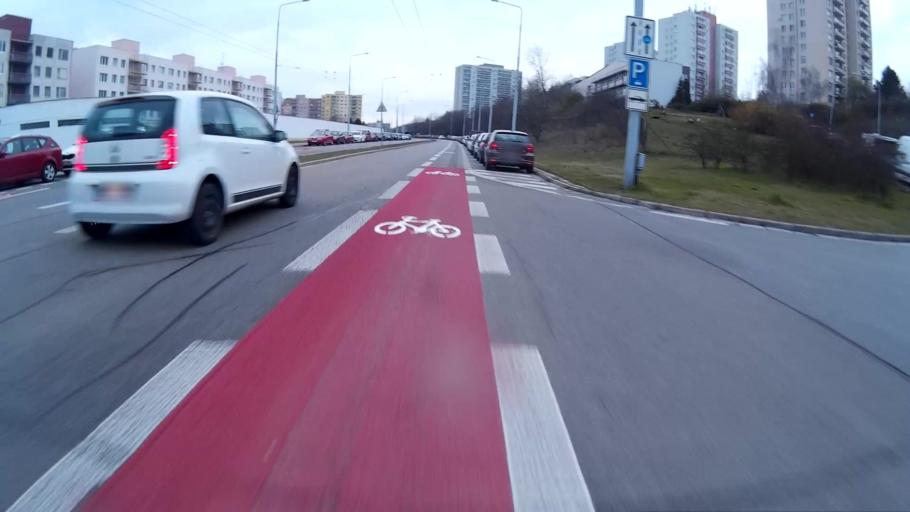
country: CZ
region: South Moravian
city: Ostopovice
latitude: 49.1770
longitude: 16.5563
